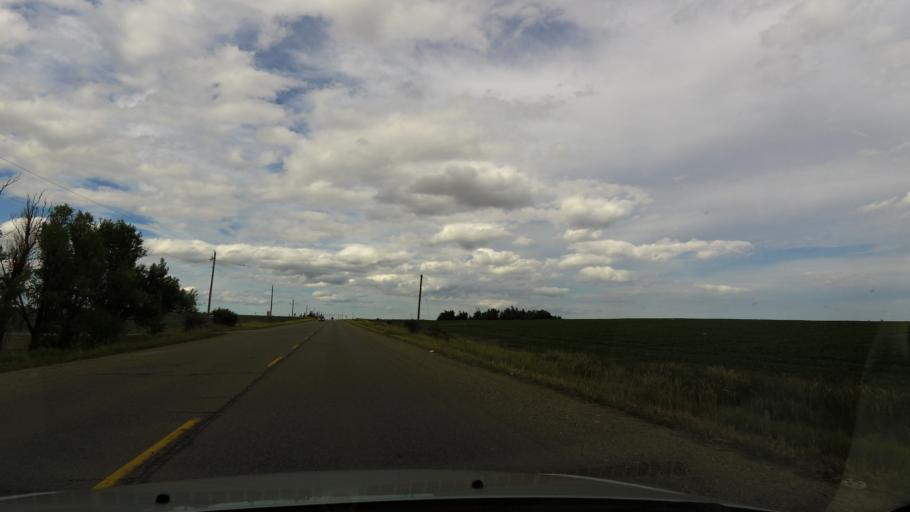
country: CA
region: Ontario
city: Brampton
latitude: 43.6705
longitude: -79.8937
